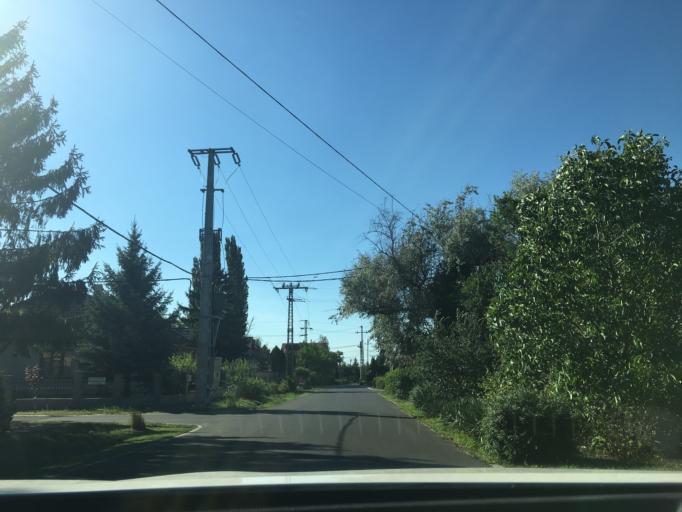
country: HU
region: Budapest
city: Budapest XVII. keruelet
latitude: 47.4768
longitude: 19.2758
